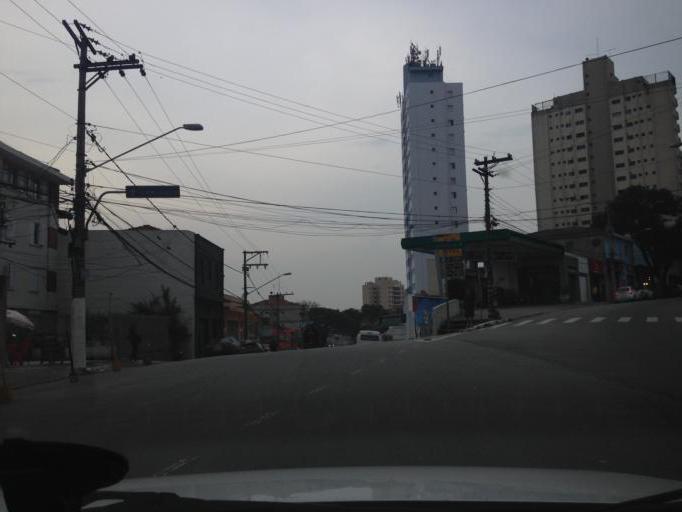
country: BR
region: Sao Paulo
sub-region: Osasco
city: Osasco
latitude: -23.5339
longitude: -46.7186
